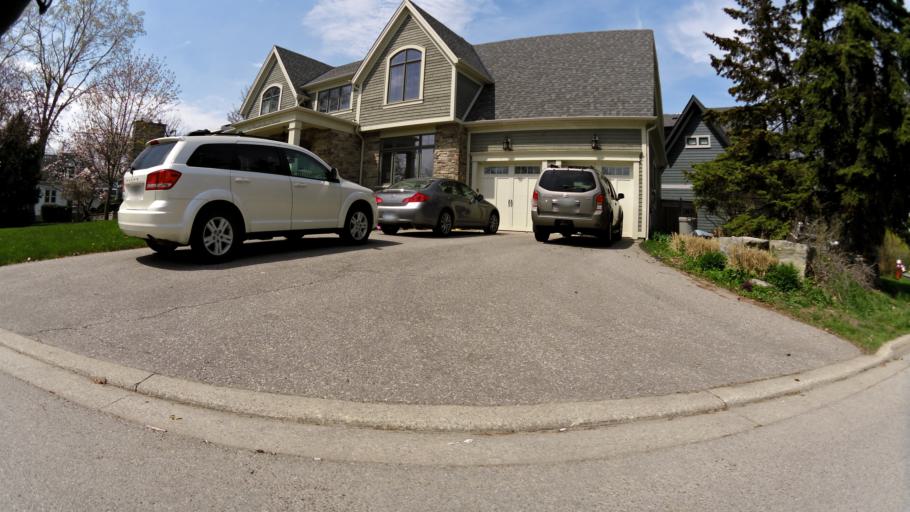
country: CA
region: Ontario
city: Mississauga
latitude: 43.5587
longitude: -79.5713
